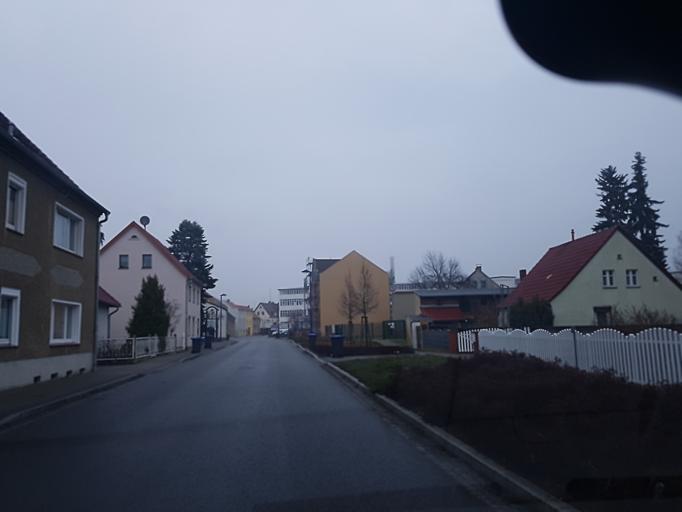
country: DE
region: Brandenburg
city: Finsterwalde
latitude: 51.6252
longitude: 13.7049
